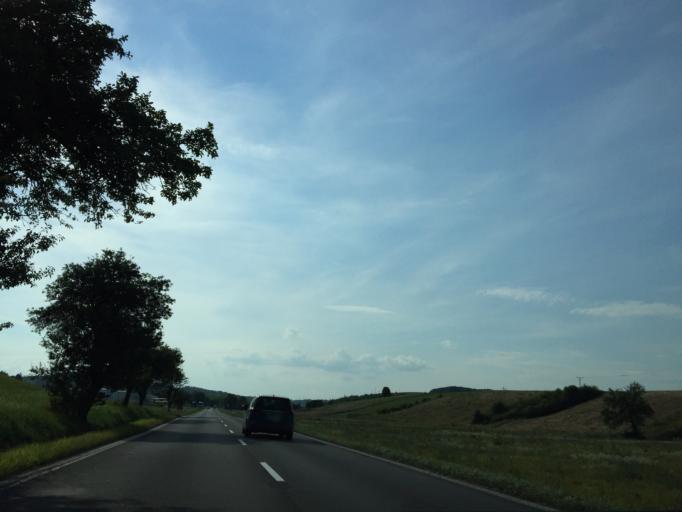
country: SK
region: Presovsky
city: Giraltovce
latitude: 49.0341
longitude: 21.4678
